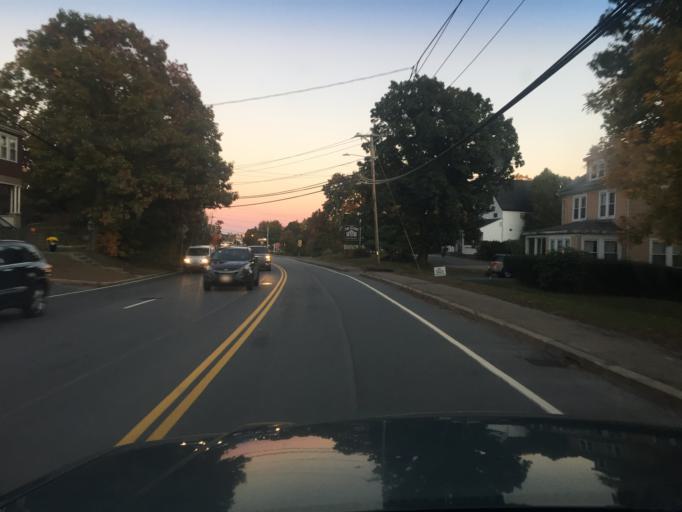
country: US
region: Massachusetts
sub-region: Worcester County
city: Milford
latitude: 42.1492
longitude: -71.4991
